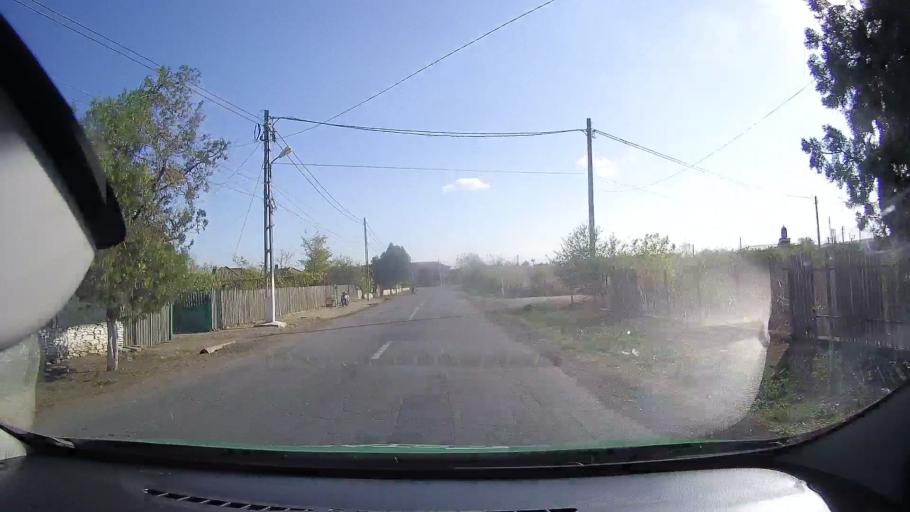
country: RO
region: Constanta
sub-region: Comuna Mihai Viteazu
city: Mihai Viteazu
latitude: 44.6305
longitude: 28.7305
